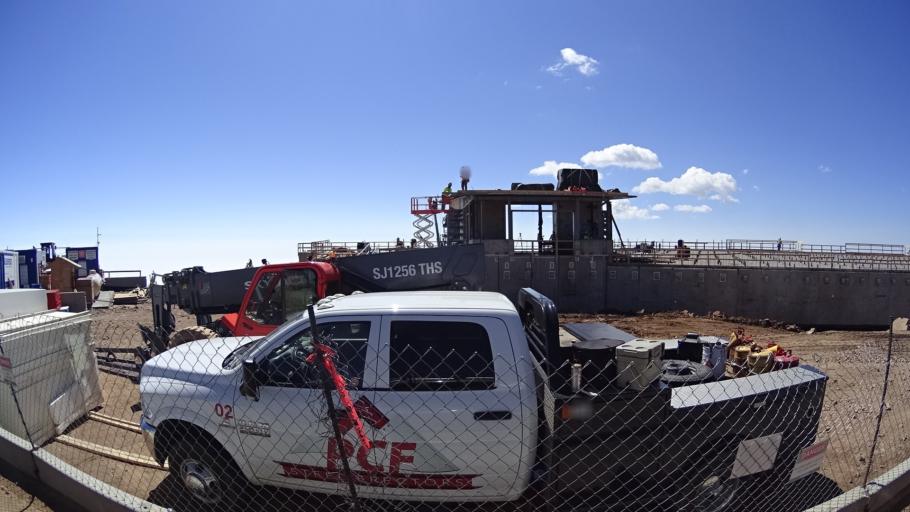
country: US
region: Colorado
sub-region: El Paso County
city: Cascade-Chipita Park
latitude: 38.8402
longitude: -105.0429
